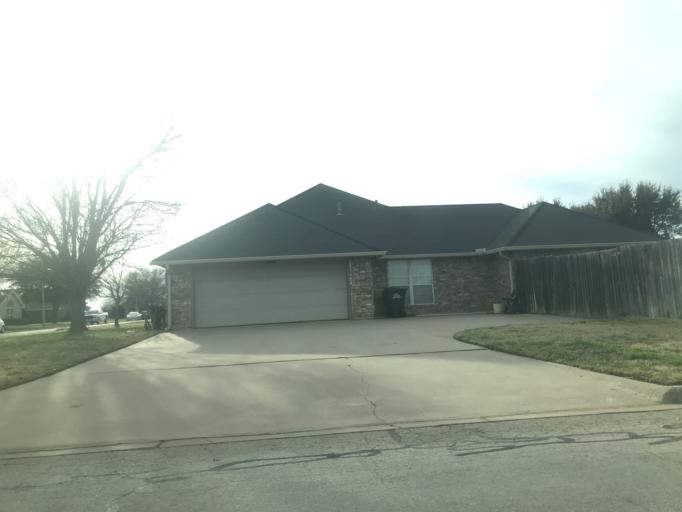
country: US
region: Texas
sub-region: Taylor County
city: Abilene
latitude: 32.3961
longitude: -99.7733
